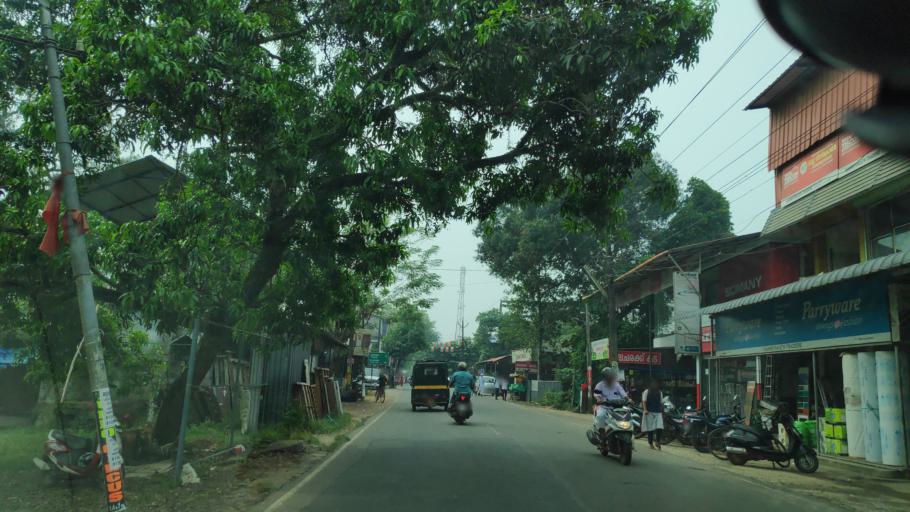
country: IN
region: Kerala
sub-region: Alappuzha
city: Alleppey
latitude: 9.5735
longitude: 76.3479
